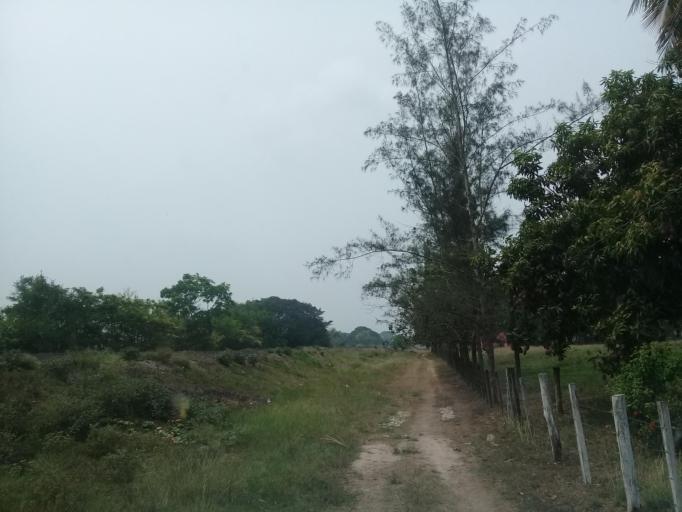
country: MX
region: Veracruz
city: Jamapa
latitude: 18.9509
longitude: -96.1976
